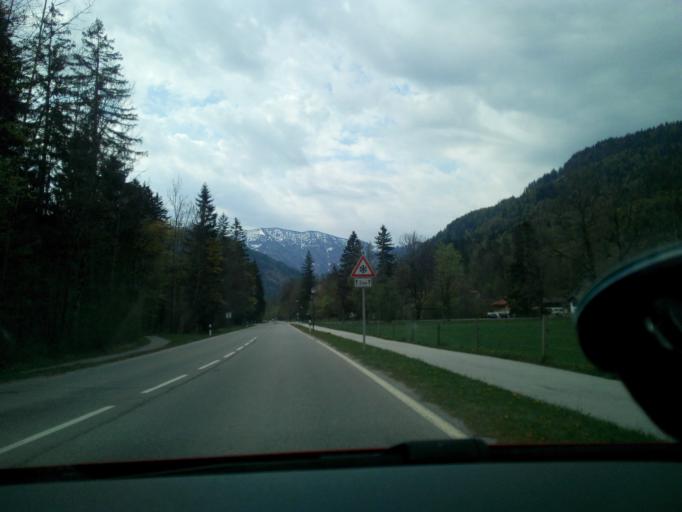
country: DE
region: Bavaria
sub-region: Upper Bavaria
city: Kreuth
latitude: 47.6413
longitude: 11.7446
